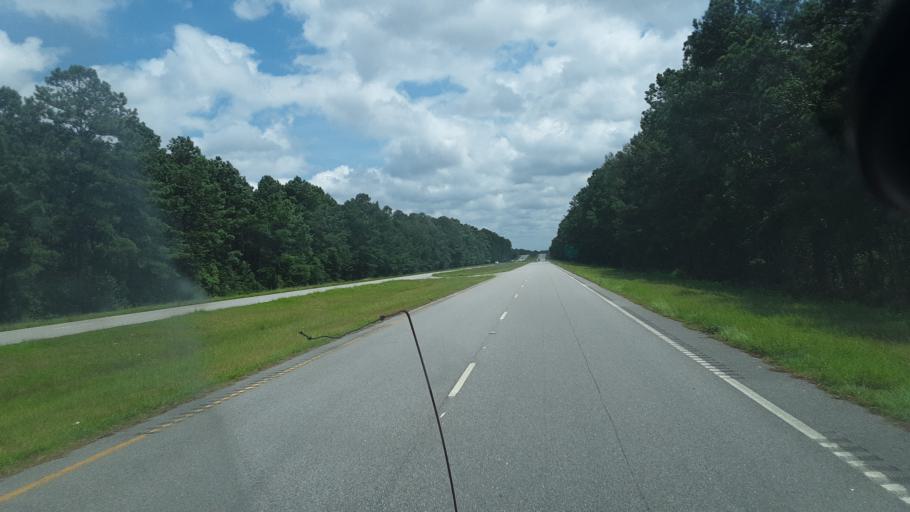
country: US
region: South Carolina
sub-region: Horry County
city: Loris
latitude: 34.0864
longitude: -78.8868
